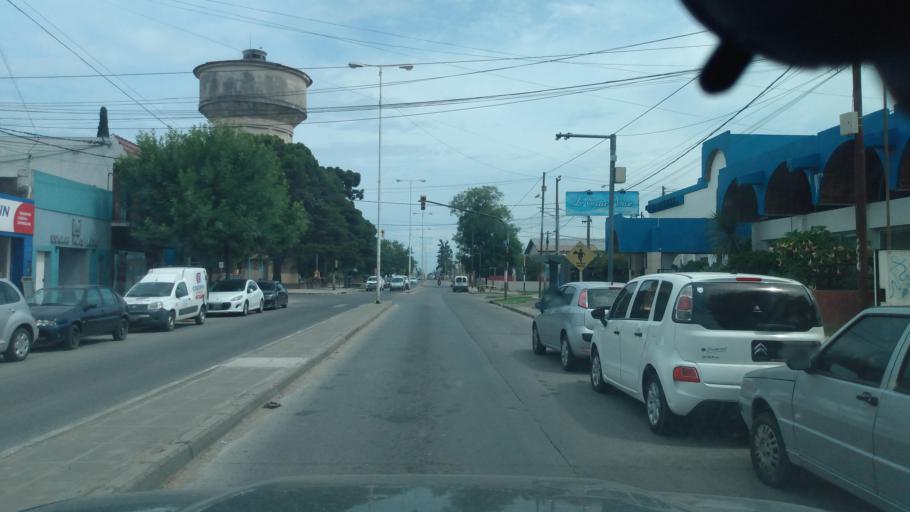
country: AR
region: Buenos Aires
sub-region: Partido de Lujan
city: Lujan
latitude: -34.5727
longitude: -59.0921
